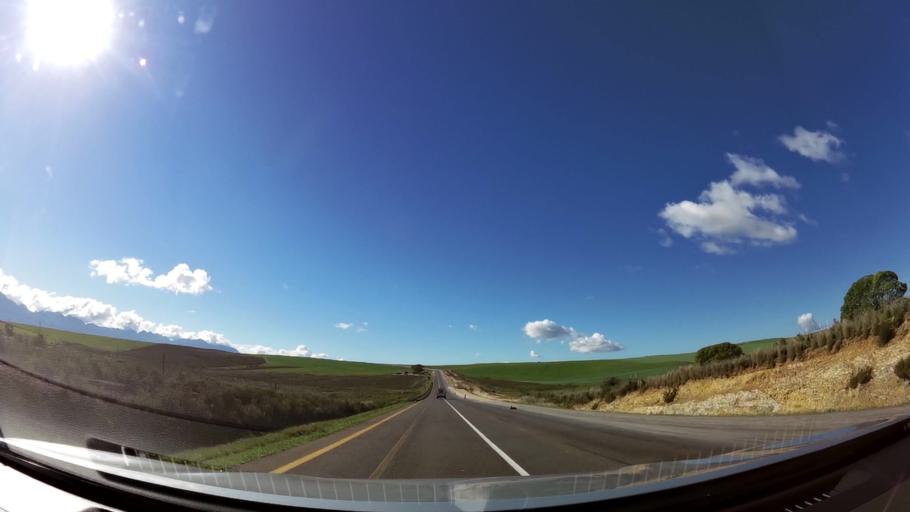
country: ZA
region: Western Cape
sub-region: Overberg District Municipality
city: Caledon
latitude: -34.1986
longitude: 19.6296
